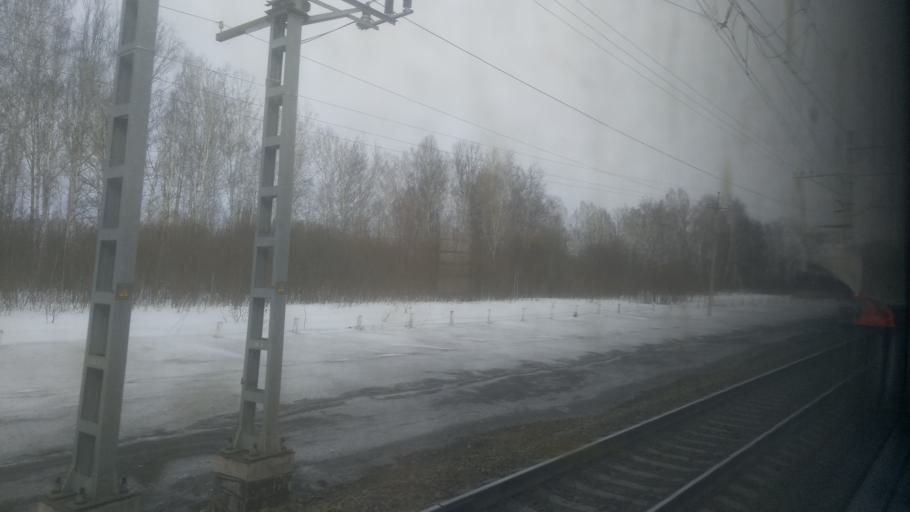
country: RU
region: Novosibirsk
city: Stantsionno-Oyashinskiy
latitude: 55.4143
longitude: 83.7678
